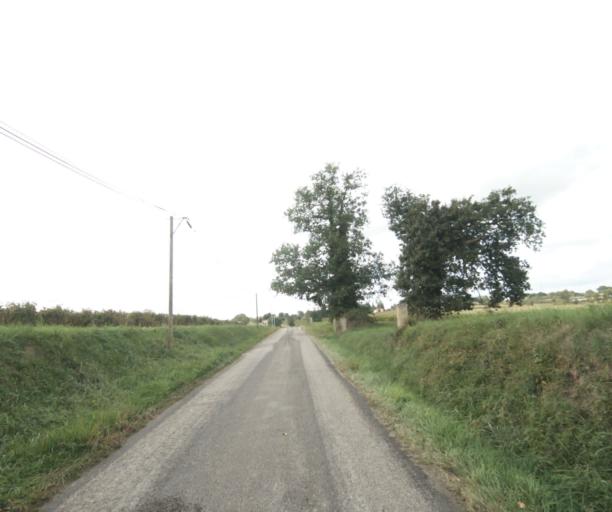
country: FR
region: Midi-Pyrenees
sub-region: Departement du Gers
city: Eauze
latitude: 43.8533
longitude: 0.0845
